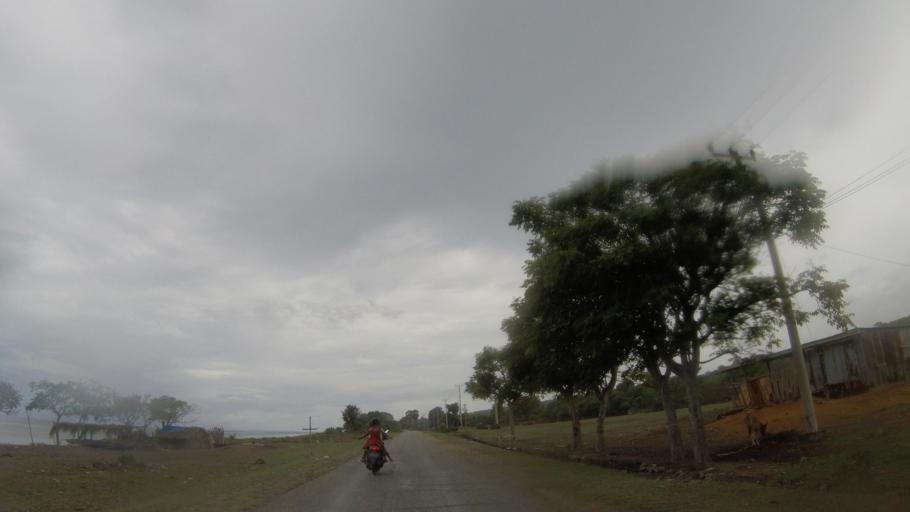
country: TL
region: Lautem
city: Lospalos
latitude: -8.3528
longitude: 126.9163
